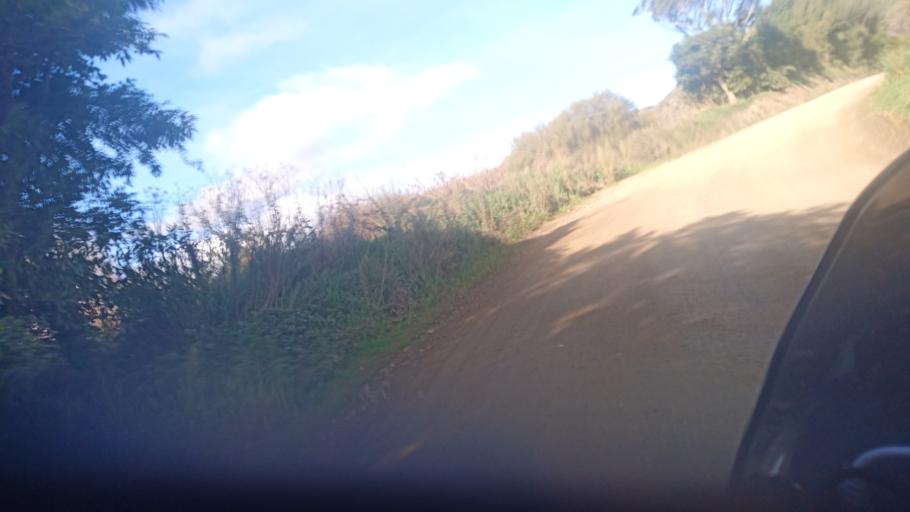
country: NZ
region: Gisborne
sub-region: Gisborne District
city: Gisborne
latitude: -38.4287
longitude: 177.5615
